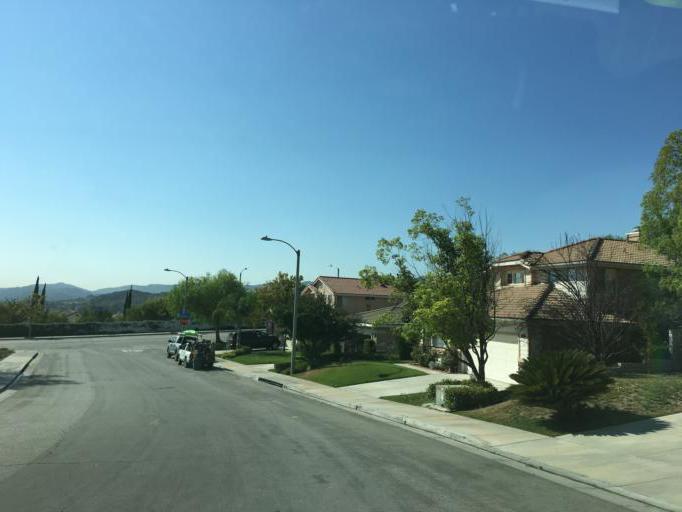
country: US
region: California
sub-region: Los Angeles County
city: Santa Clarita
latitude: 34.3887
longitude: -118.5906
